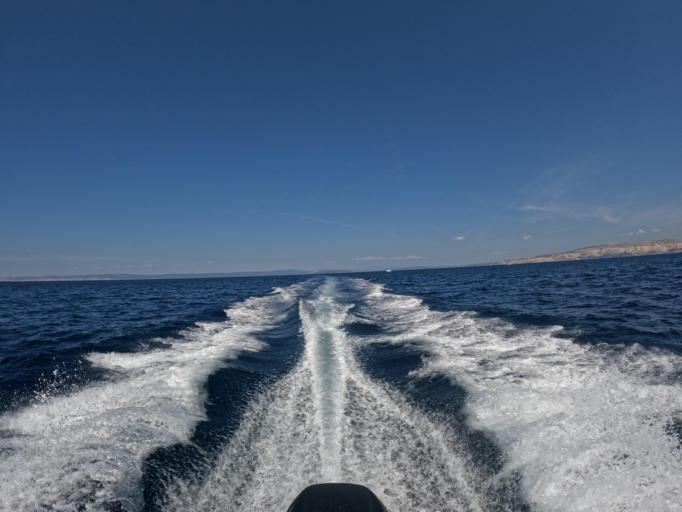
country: HR
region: Primorsko-Goranska
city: Lopar
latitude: 44.8693
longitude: 14.6731
